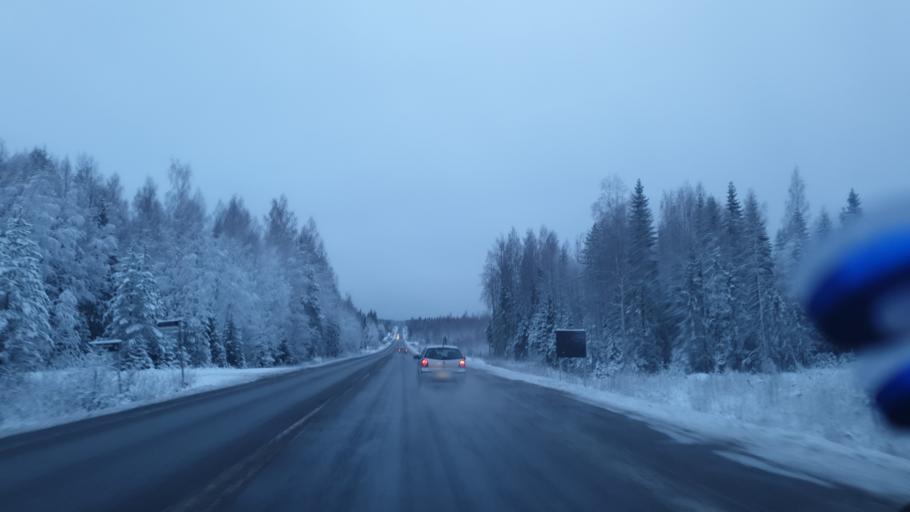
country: FI
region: Central Finland
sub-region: Saarijaervi-Viitasaari
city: Viitasaari
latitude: 63.0297
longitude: 25.8126
